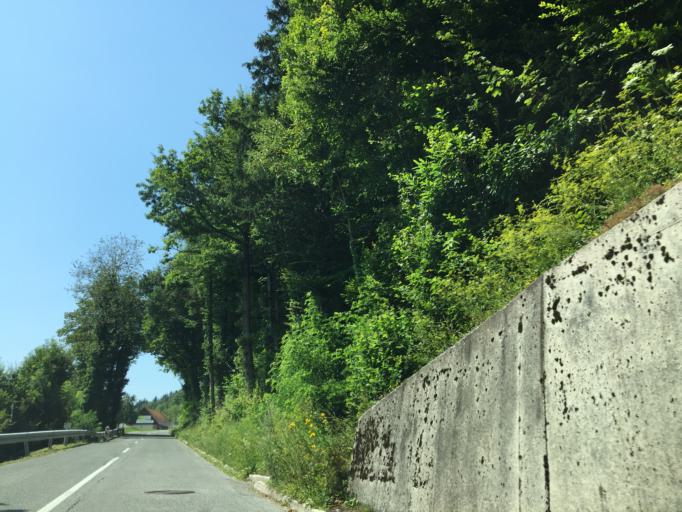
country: SI
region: Trbovlje
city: Trbovlje
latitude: 46.1862
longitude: 15.0596
